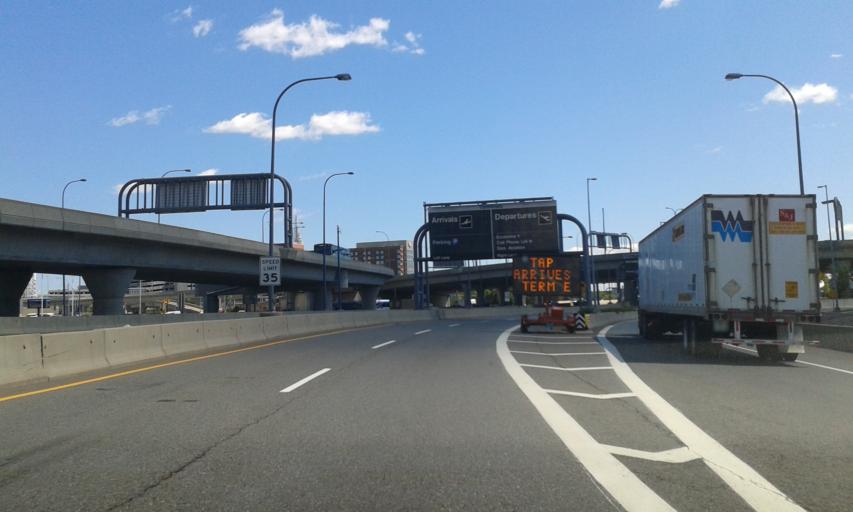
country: US
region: Massachusetts
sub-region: Suffolk County
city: Chelsea
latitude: 42.3710
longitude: -71.0278
